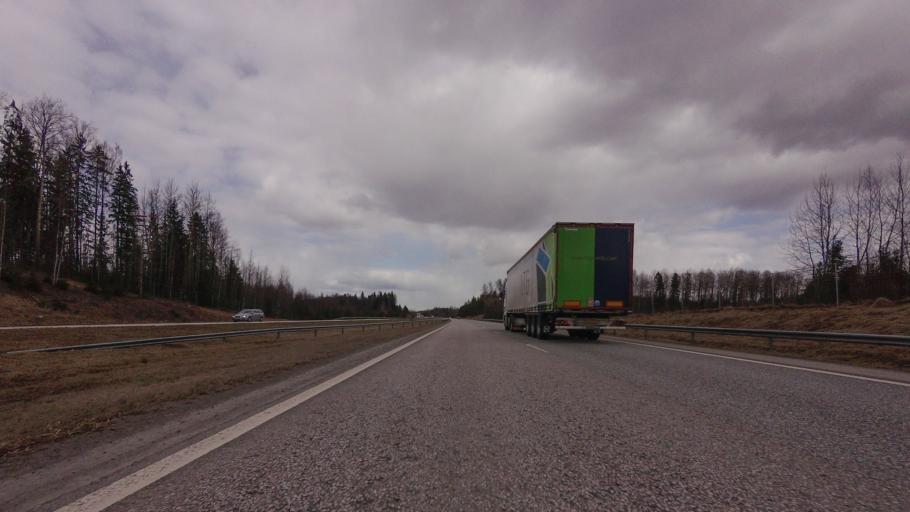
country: FI
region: Uusimaa
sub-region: Helsinki
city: Nurmijaervi
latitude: 60.3744
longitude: 24.8134
